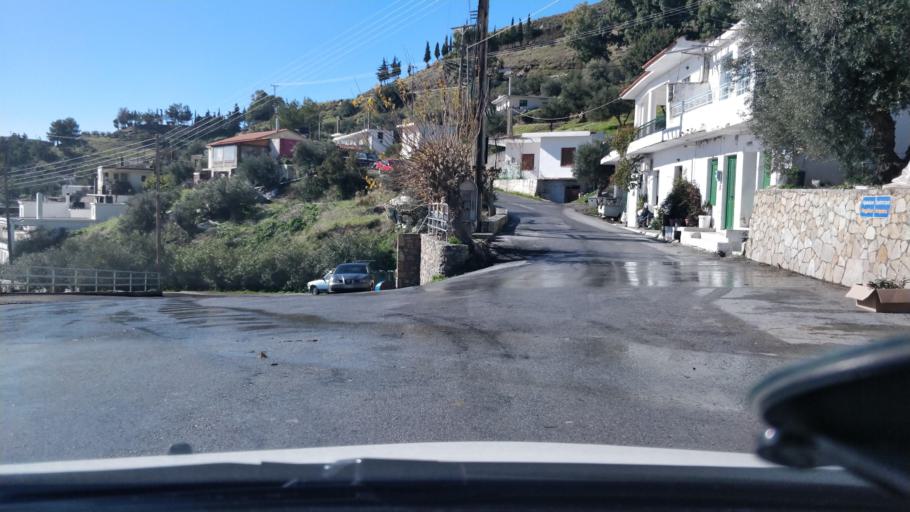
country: GR
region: Crete
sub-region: Nomos Irakleiou
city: Kastelli
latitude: 35.0416
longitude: 25.4452
